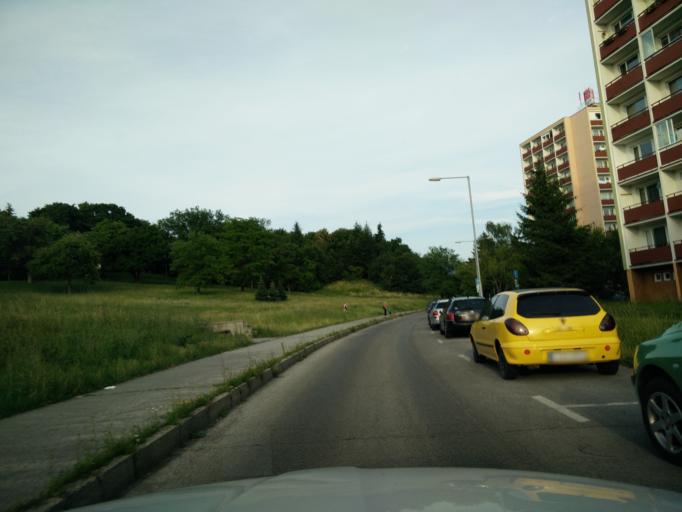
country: SK
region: Nitriansky
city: Prievidza
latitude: 48.7707
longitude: 18.6315
